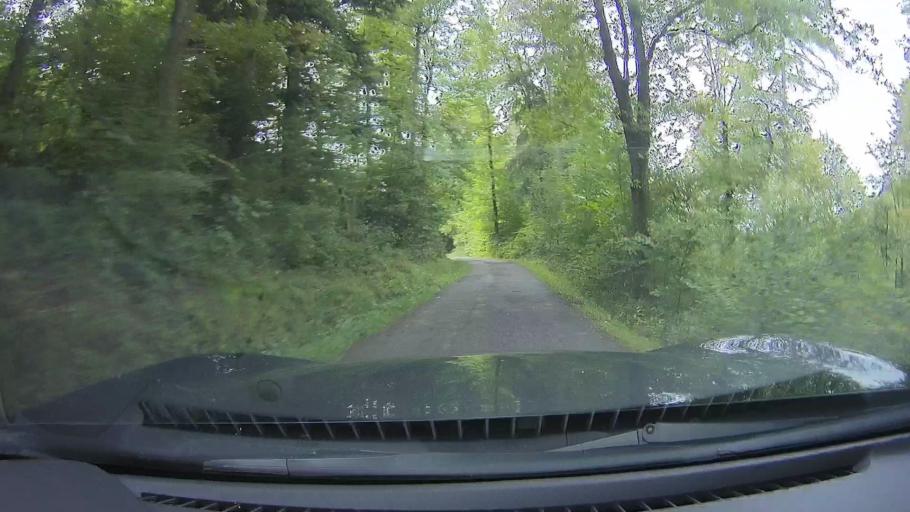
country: DE
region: Baden-Wuerttemberg
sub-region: Regierungsbezirk Stuttgart
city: Wustenrot
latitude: 49.0671
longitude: 9.4679
